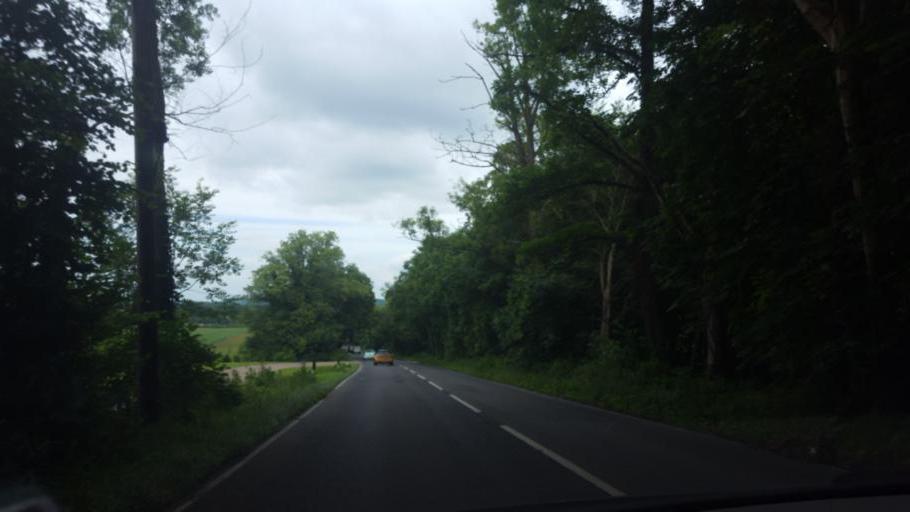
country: GB
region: England
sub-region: Royal Borough of Windsor and Maidenhead
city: Hurley
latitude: 51.5380
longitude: -0.8409
